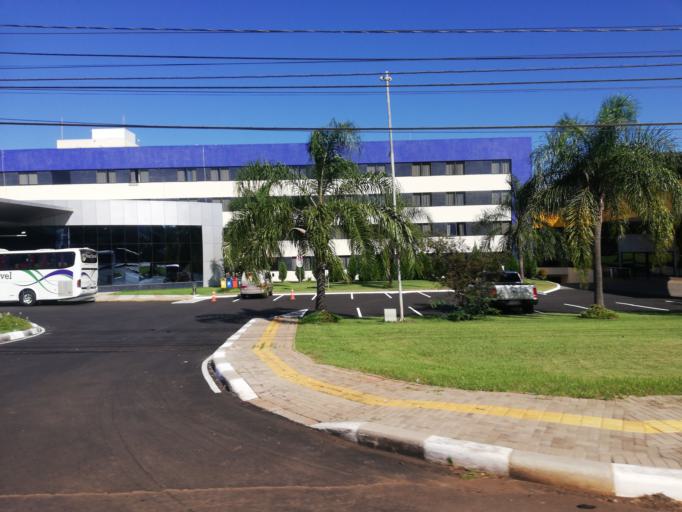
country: BR
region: Parana
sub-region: Foz Do Iguacu
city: Foz do Iguacu
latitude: -25.5608
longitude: -54.5617
